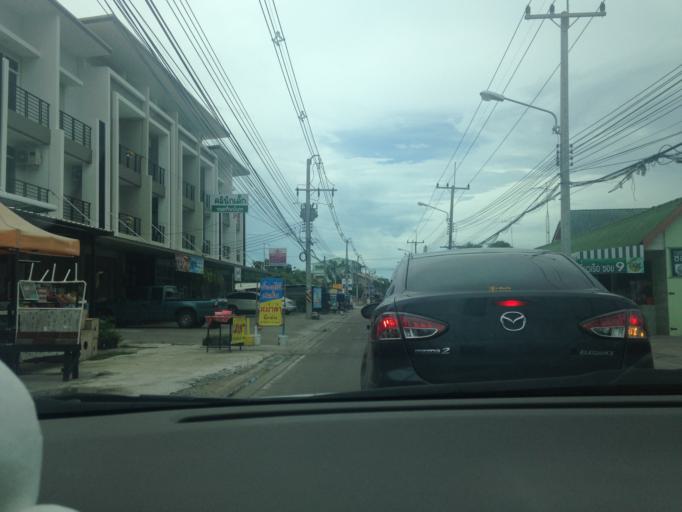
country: TH
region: Chon Buri
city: Chon Buri
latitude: 13.3216
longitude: 100.9286
